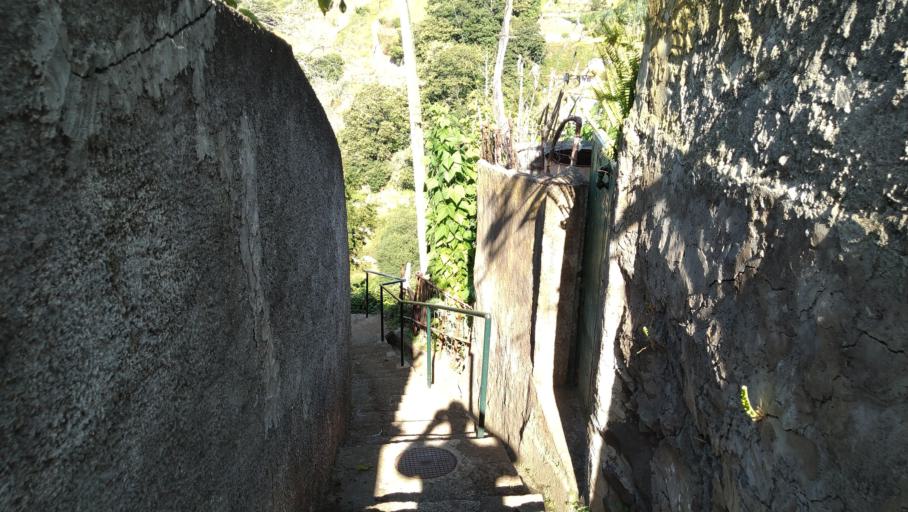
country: PT
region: Madeira
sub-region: Funchal
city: Nossa Senhora do Monte
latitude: 32.6812
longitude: -16.9392
